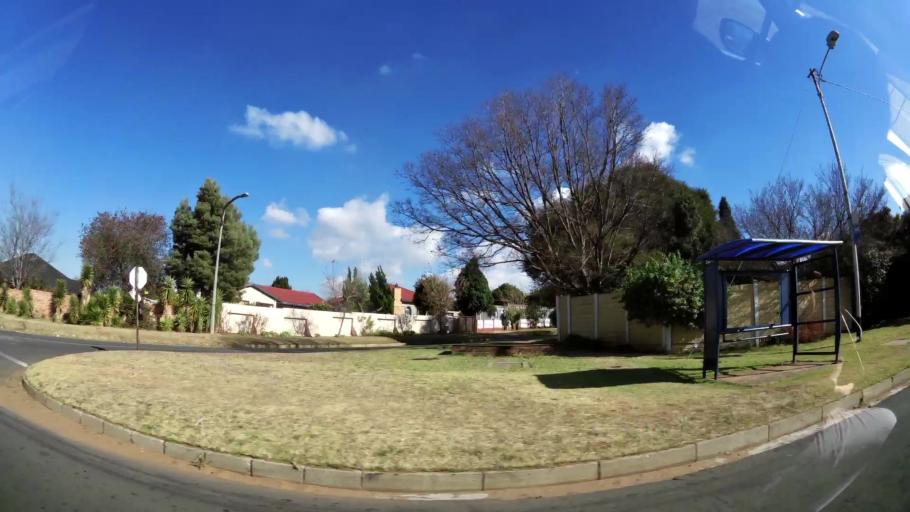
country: ZA
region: Gauteng
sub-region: City of Johannesburg Metropolitan Municipality
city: Roodepoort
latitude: -26.1502
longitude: 27.8330
